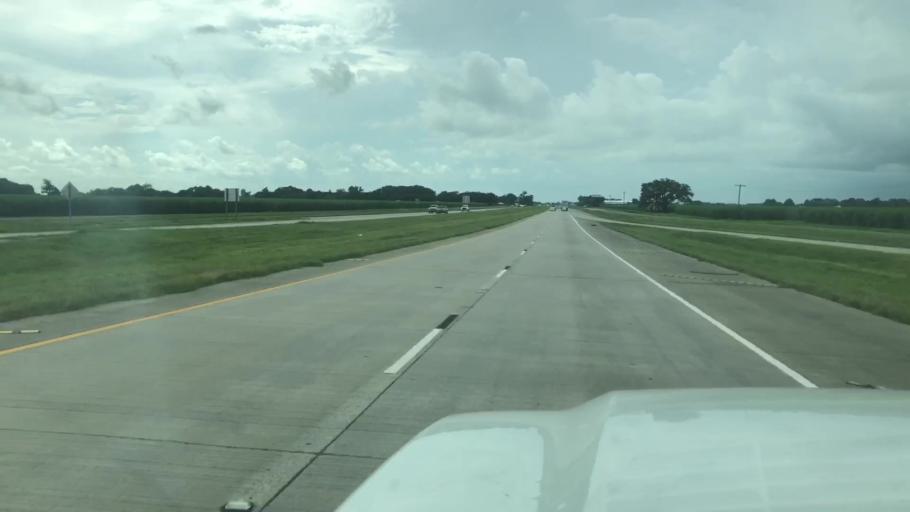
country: US
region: Louisiana
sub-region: Iberia Parish
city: Jeanerette
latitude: 29.9215
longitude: -91.7311
